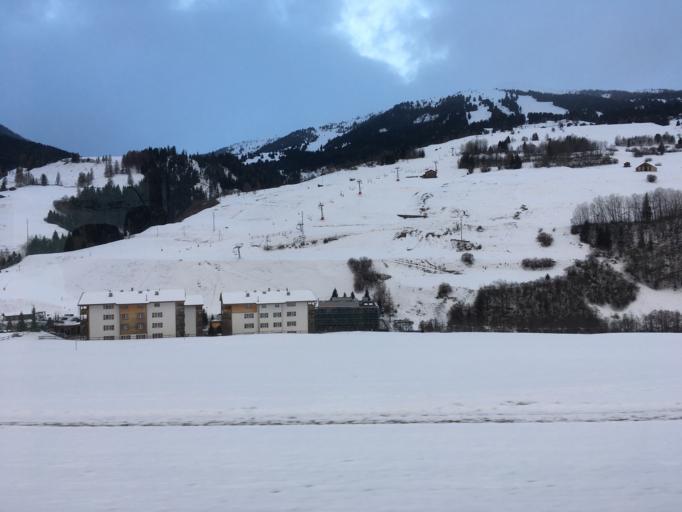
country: CH
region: Grisons
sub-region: Albula District
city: Tiefencastel
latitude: 46.5996
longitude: 9.5946
